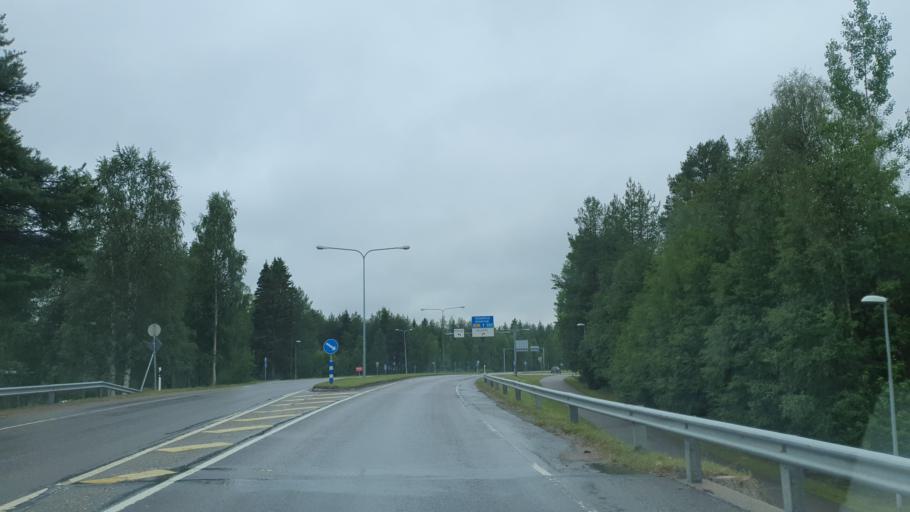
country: FI
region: Lapland
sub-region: Itae-Lappi
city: Kemijaervi
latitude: 66.7188
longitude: 27.3883
